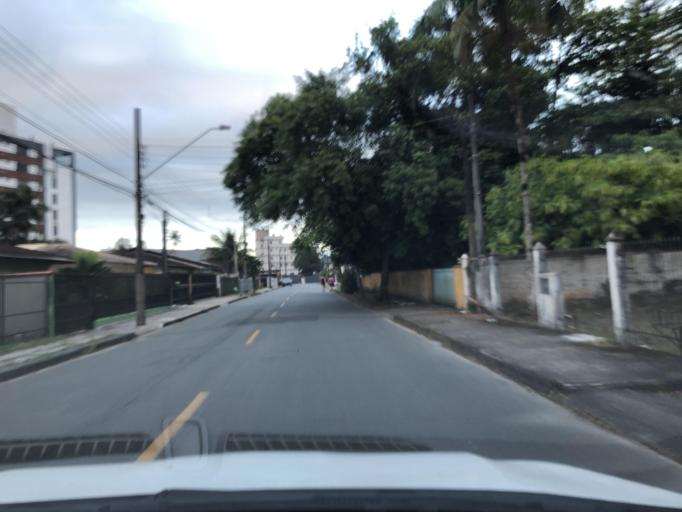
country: BR
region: Santa Catarina
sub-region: Joinville
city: Joinville
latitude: -26.2697
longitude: -48.8644
